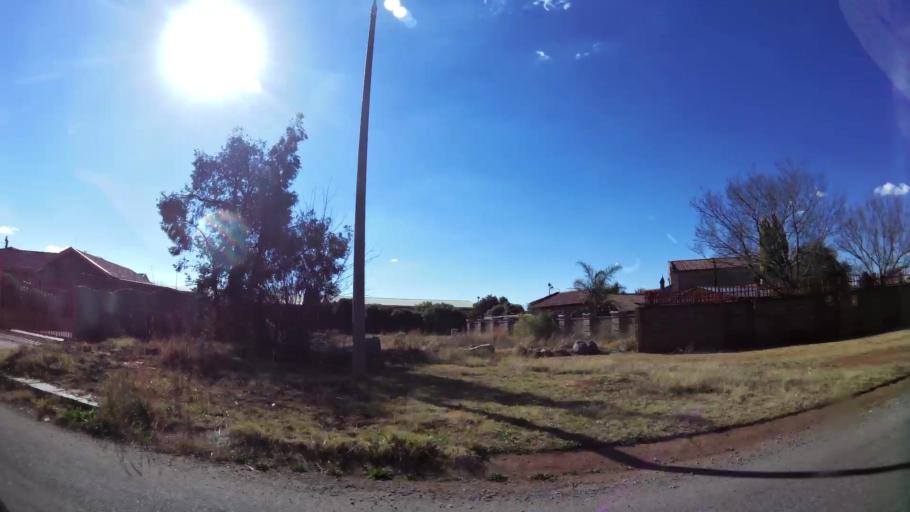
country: ZA
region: Gauteng
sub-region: West Rand District Municipality
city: Carletonville
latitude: -26.3579
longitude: 27.3722
